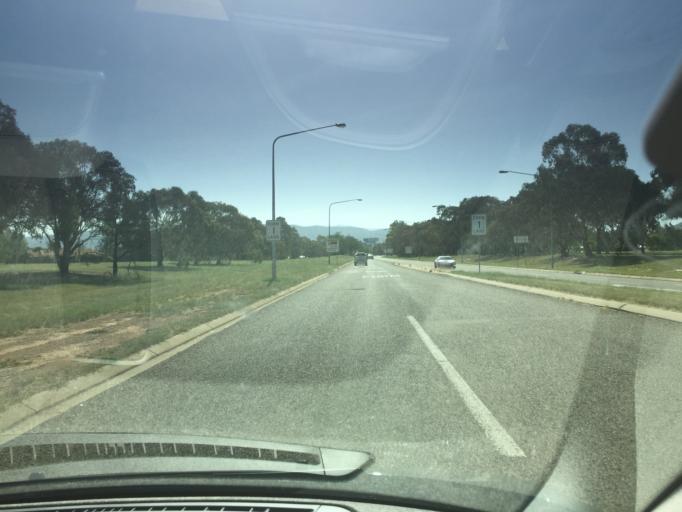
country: AU
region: Australian Capital Territory
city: Macarthur
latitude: -35.4238
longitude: 149.0888
